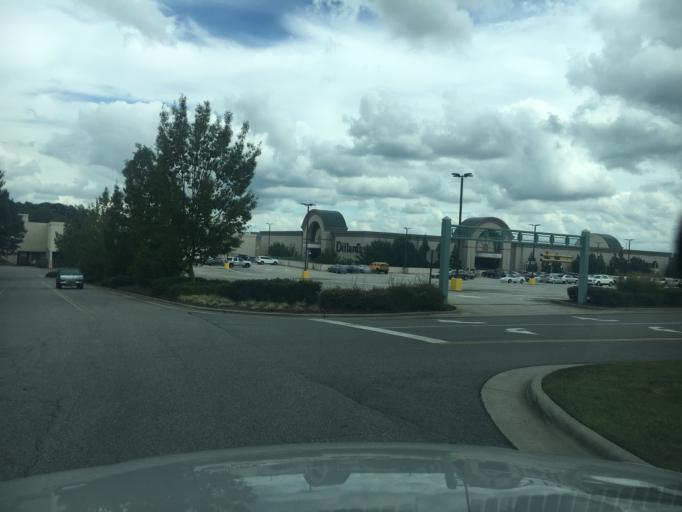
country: US
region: North Carolina
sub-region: Catawba County
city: Hickory
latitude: 35.7039
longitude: -81.3084
